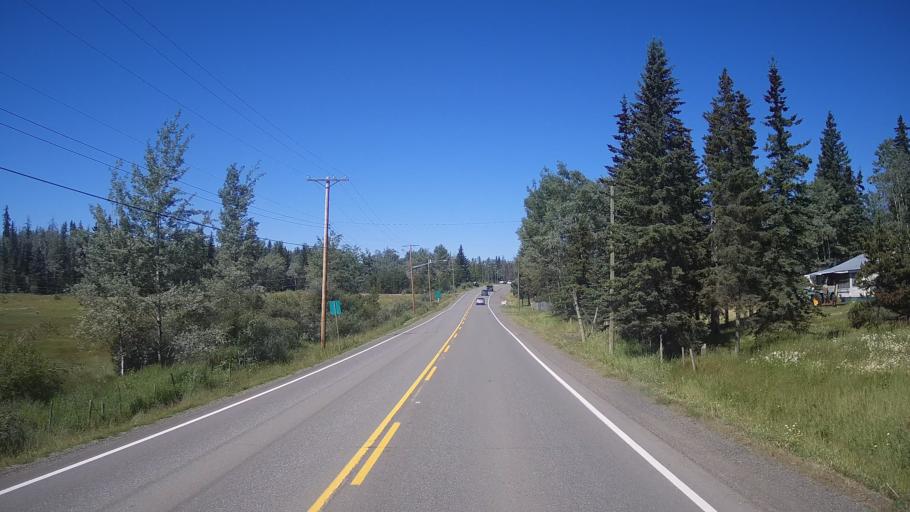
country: CA
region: British Columbia
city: Cache Creek
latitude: 51.5547
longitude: -121.2119
